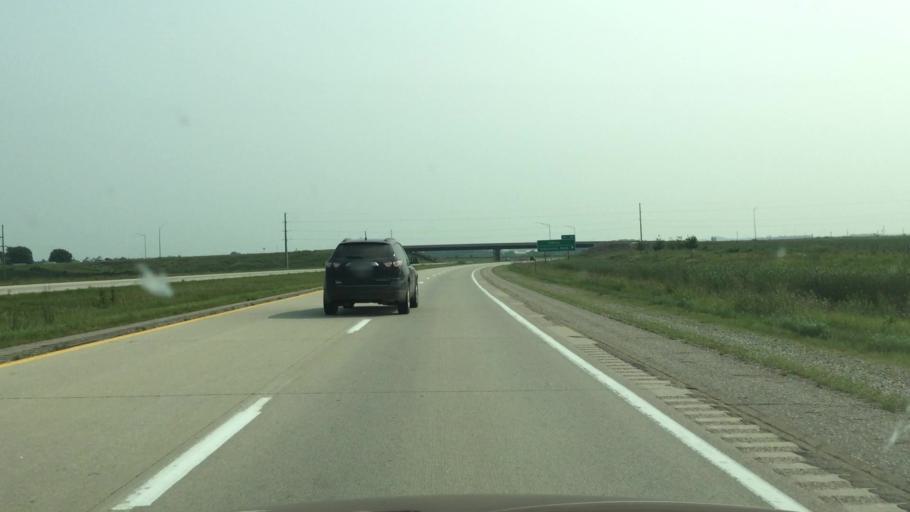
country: US
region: Iowa
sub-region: Osceola County
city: Sibley
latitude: 43.3800
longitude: -95.7548
